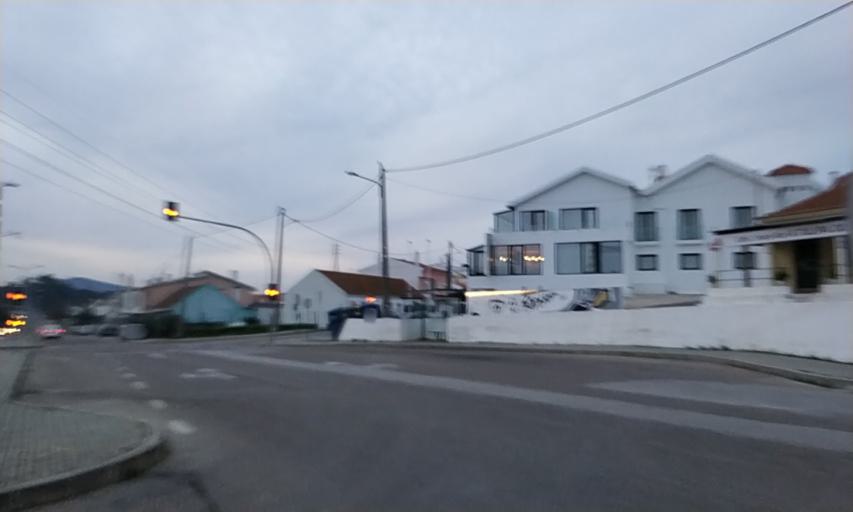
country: PT
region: Setubal
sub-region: Setubal
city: Setubal
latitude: 38.5225
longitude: -8.8507
